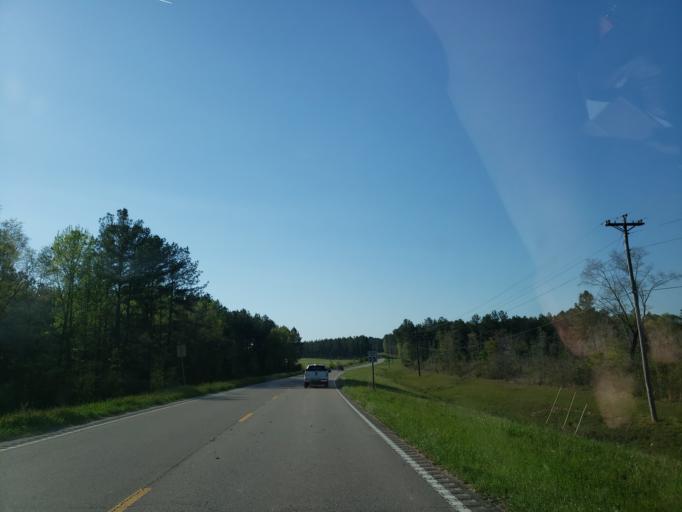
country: US
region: Mississippi
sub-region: Perry County
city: Richton
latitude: 31.4726
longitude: -89.0015
